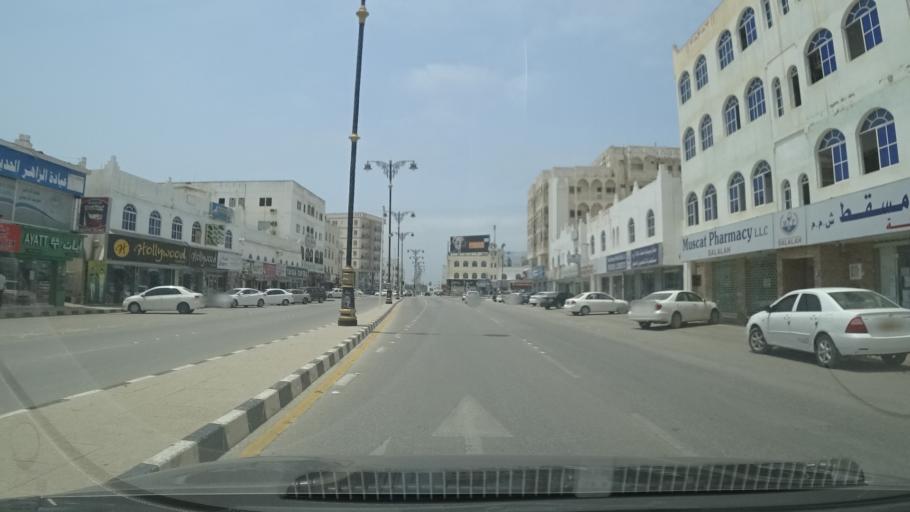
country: OM
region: Zufar
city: Salalah
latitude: 17.0139
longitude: 54.0933
